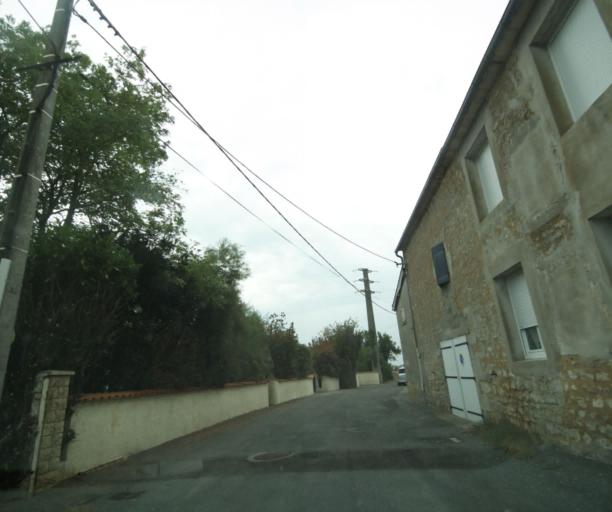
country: FR
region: Poitou-Charentes
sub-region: Departement de la Charente-Maritime
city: Tonnay-Charente
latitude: 45.9514
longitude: -0.9262
